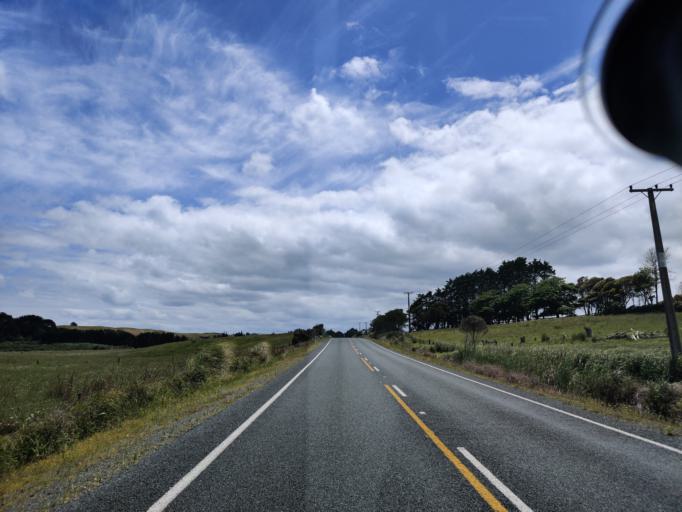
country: NZ
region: Northland
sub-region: Far North District
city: Kaitaia
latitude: -34.7313
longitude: 173.0448
